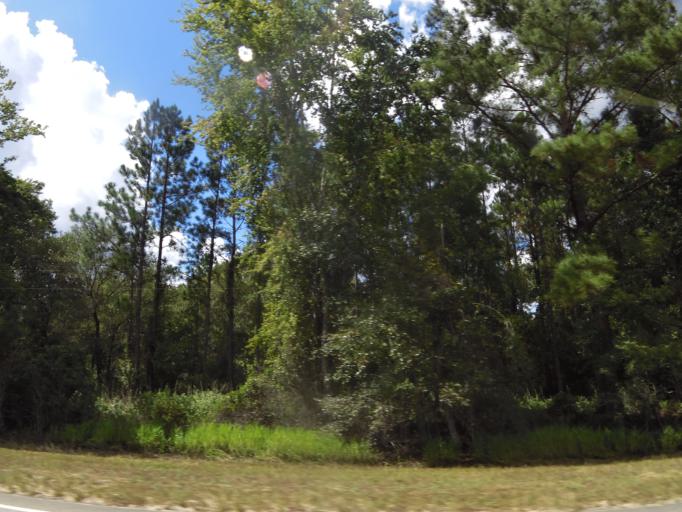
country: US
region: Georgia
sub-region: Charlton County
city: Folkston
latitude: 30.9404
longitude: -82.0224
